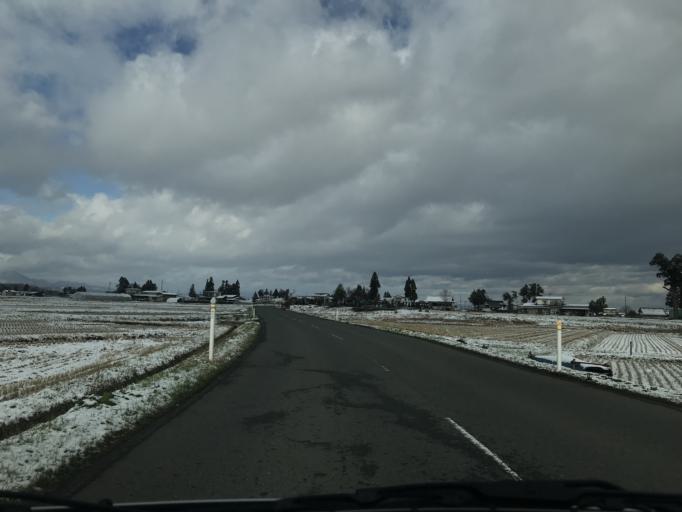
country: JP
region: Iwate
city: Mizusawa
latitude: 39.1563
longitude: 141.1133
